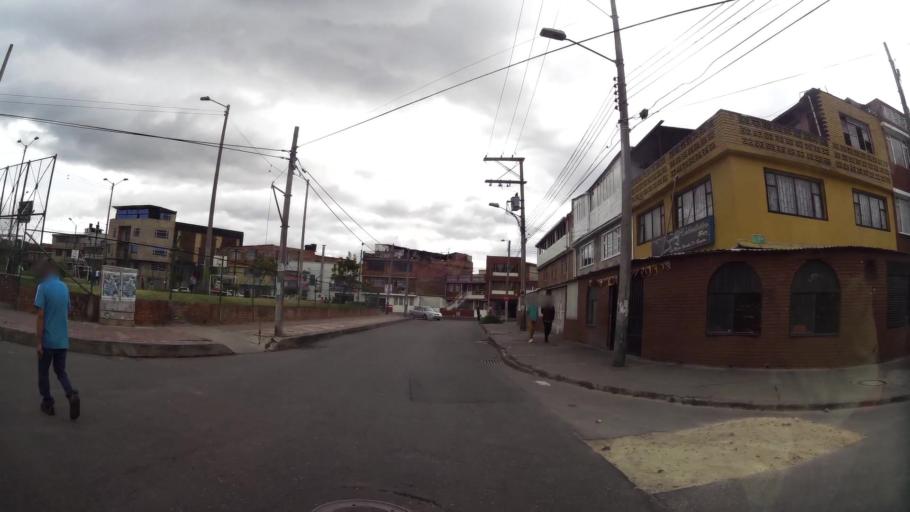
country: CO
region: Bogota D.C.
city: Bogota
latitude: 4.5982
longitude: -74.1427
